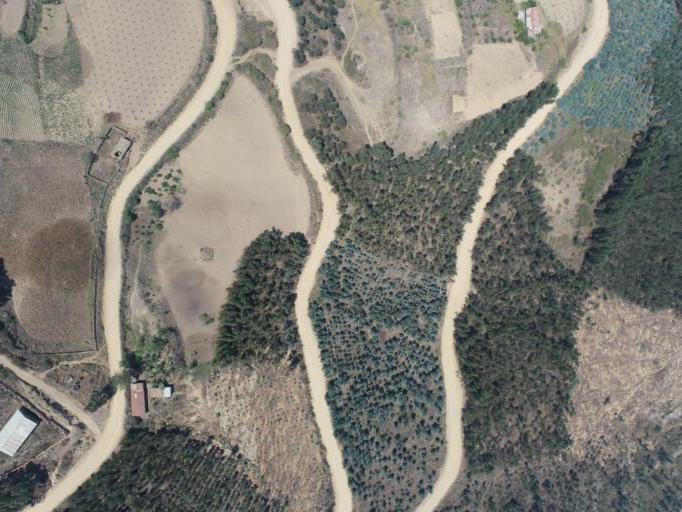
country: BO
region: La Paz
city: Quime
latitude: -16.9028
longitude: -67.1395
